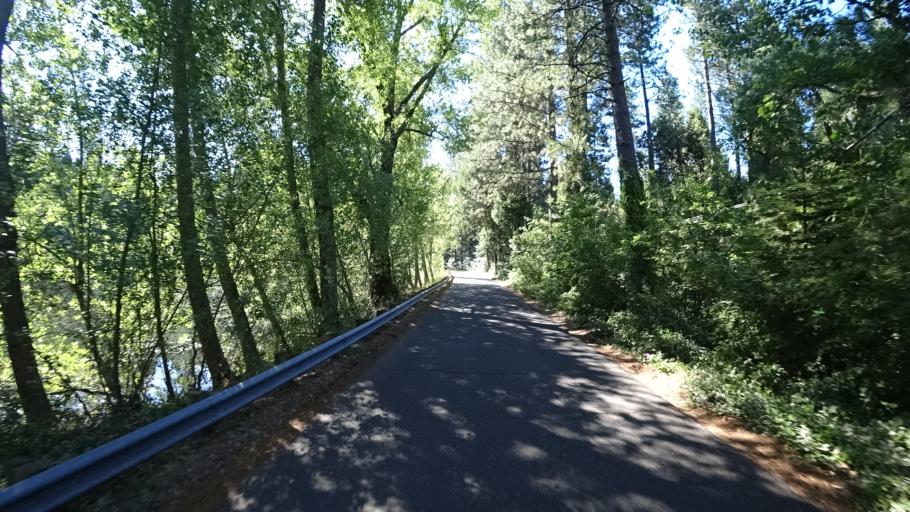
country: US
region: California
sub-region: Calaveras County
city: Arnold
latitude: 38.2380
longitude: -120.3658
